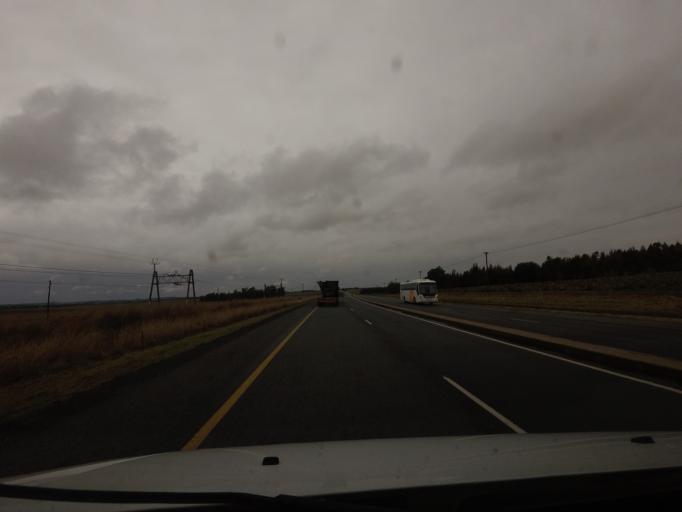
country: ZA
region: Mpumalanga
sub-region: Nkangala District Municipality
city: Belfast
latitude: -25.7292
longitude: 30.0232
